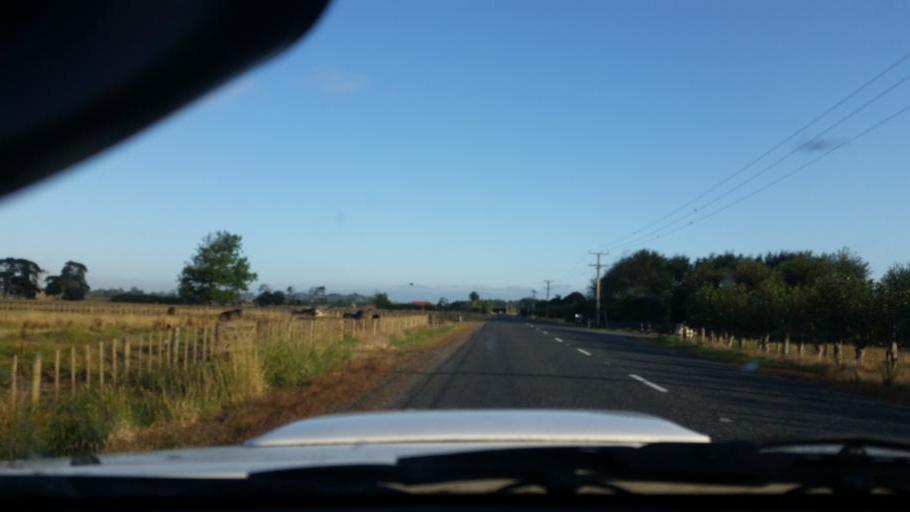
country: NZ
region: Northland
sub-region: Kaipara District
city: Dargaville
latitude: -35.9940
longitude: 173.8855
